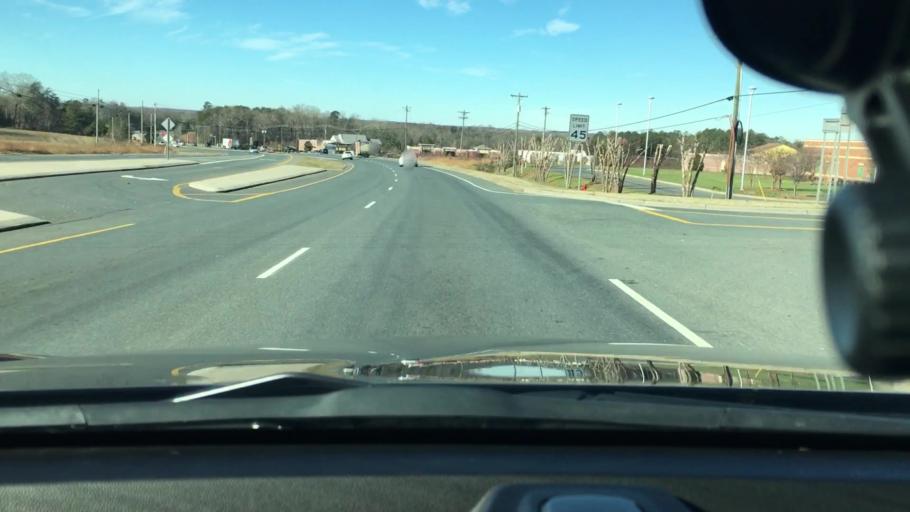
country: US
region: North Carolina
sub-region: Stanly County
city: Locust
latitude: 35.2549
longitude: -80.4544
